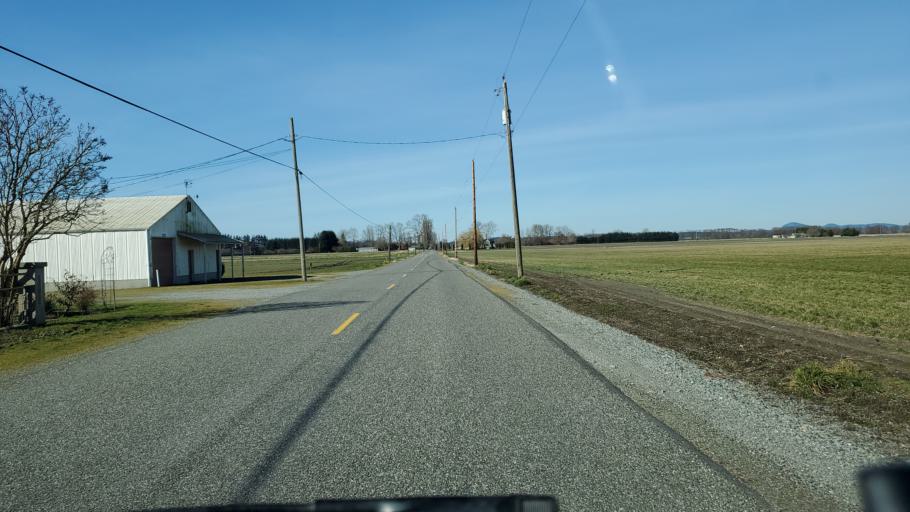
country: US
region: Washington
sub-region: Skagit County
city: Mount Vernon
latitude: 48.3703
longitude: -122.3683
